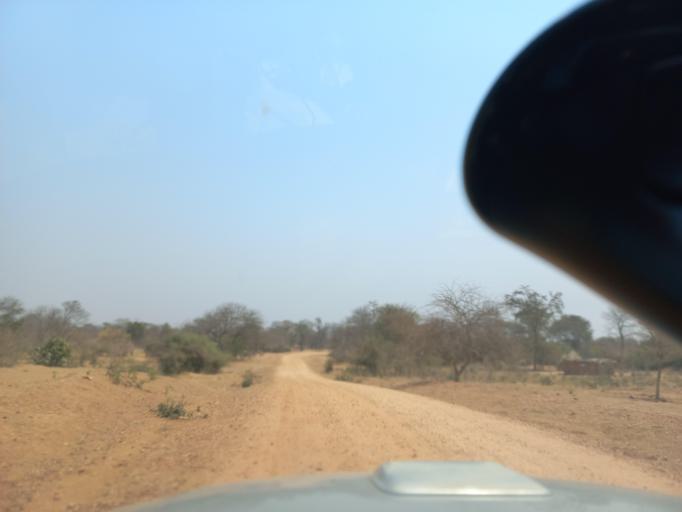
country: ZW
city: Chirundu
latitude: -15.9456
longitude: 28.8150
